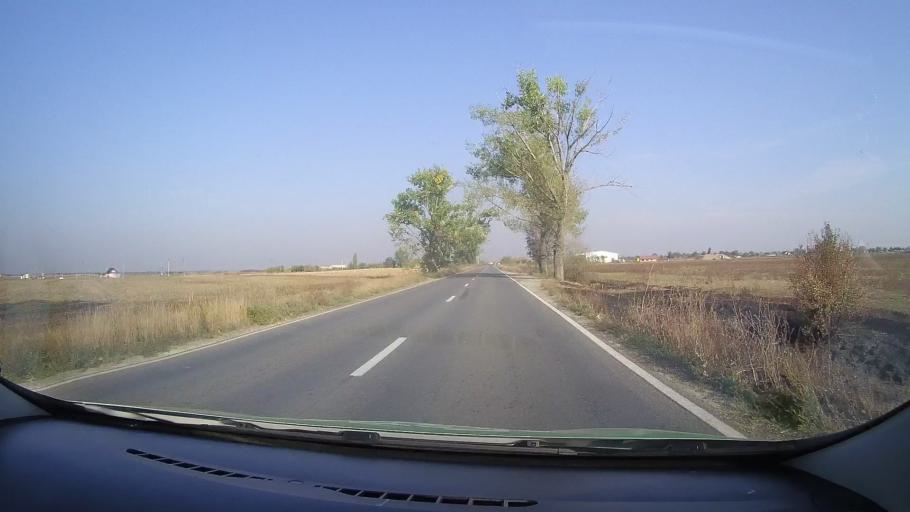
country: RO
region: Arad
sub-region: Comuna Pilu
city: Pilu
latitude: 46.5658
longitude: 21.3450
